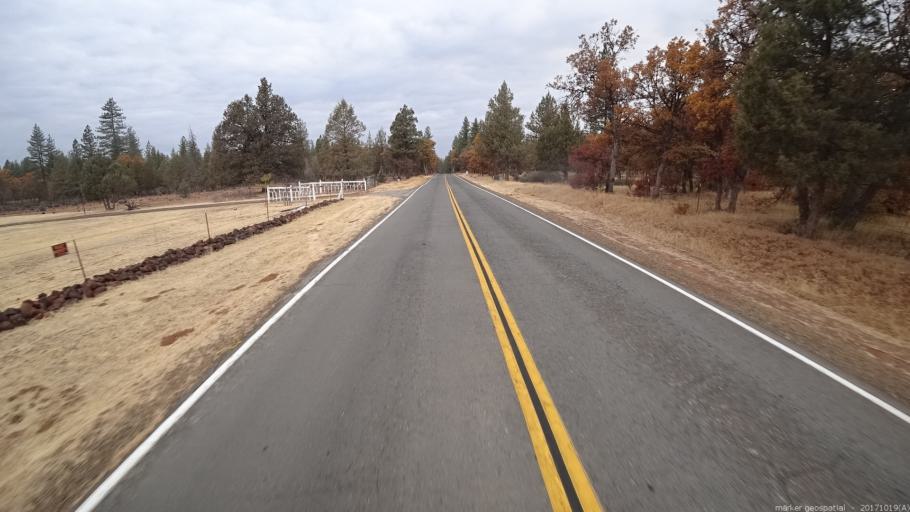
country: US
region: California
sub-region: Shasta County
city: Burney
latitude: 41.1293
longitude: -121.3384
